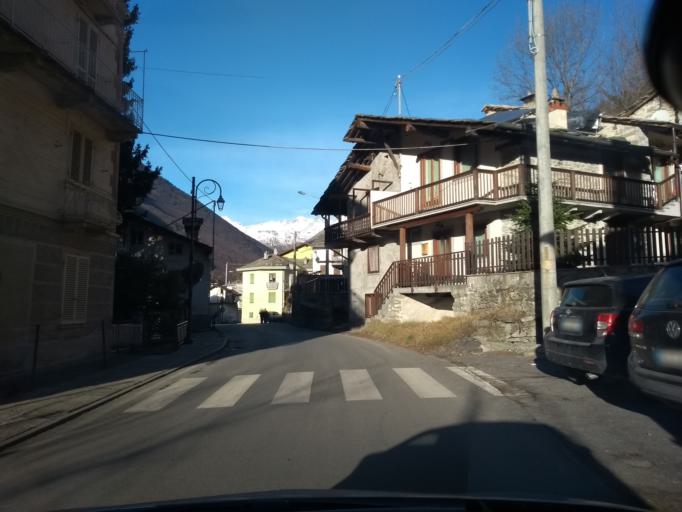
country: IT
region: Piedmont
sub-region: Provincia di Torino
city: Cantoira
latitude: 45.3402
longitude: 7.3855
